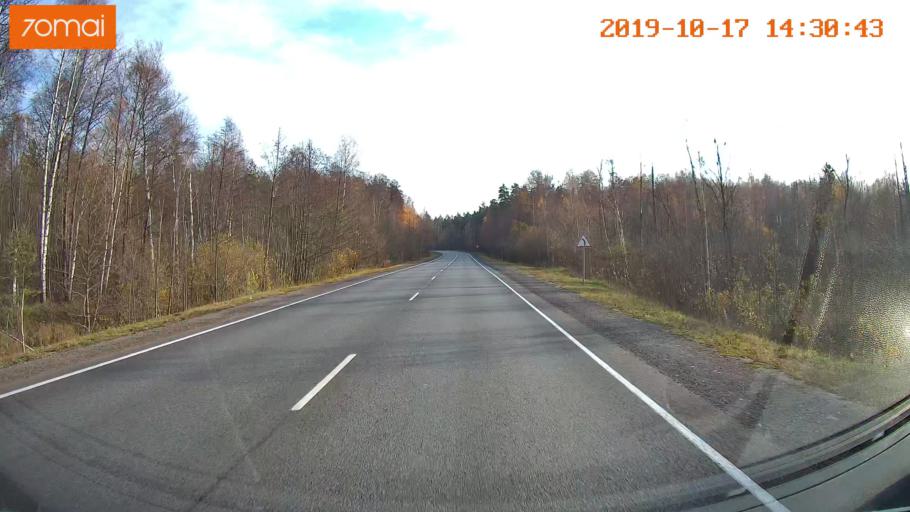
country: RU
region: Rjazan
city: Solotcha
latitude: 54.9440
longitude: 39.9492
